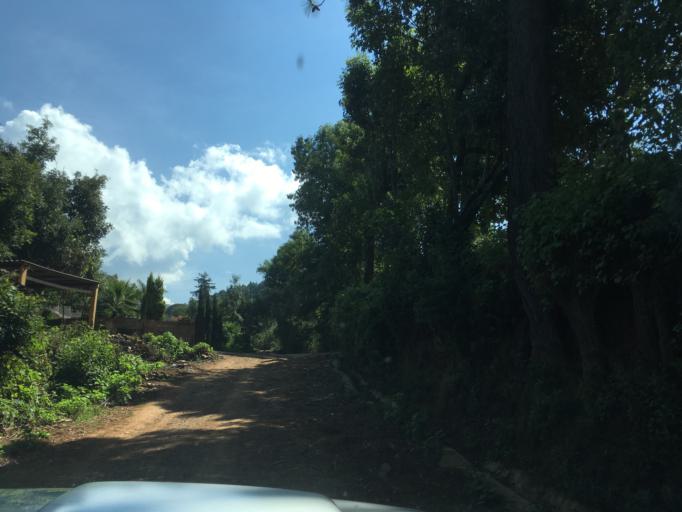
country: MX
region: Michoacan
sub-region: Zitacuaro
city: La Fundicion (Quinta Manzana)
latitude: 19.4903
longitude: -100.3149
